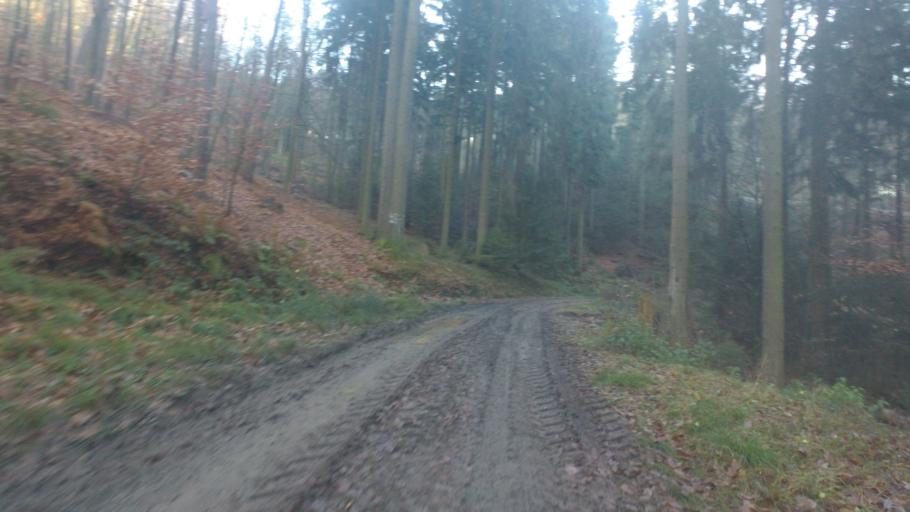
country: DE
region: Baden-Wuerttemberg
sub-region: Karlsruhe Region
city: Heiligkreuzsteinach
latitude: 49.4872
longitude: 8.8066
